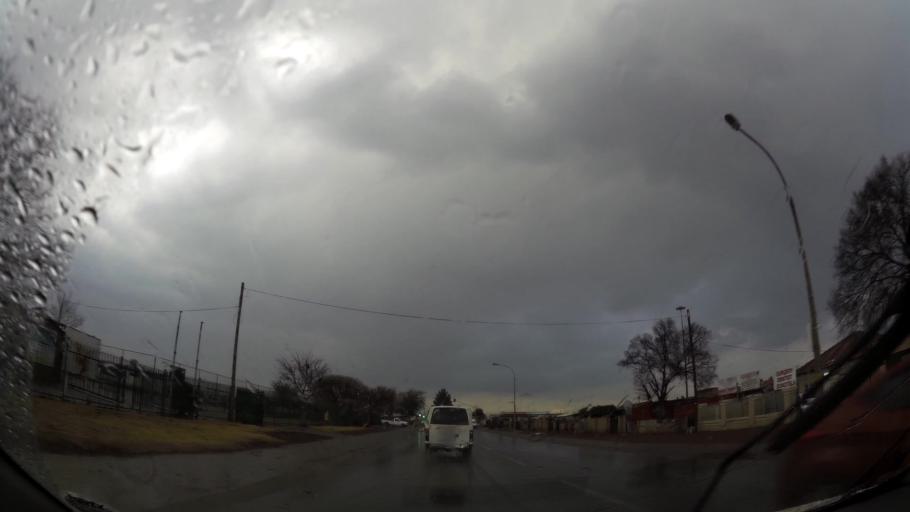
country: ZA
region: Gauteng
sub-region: Ekurhuleni Metropolitan Municipality
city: Germiston
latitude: -26.3497
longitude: 28.1339
